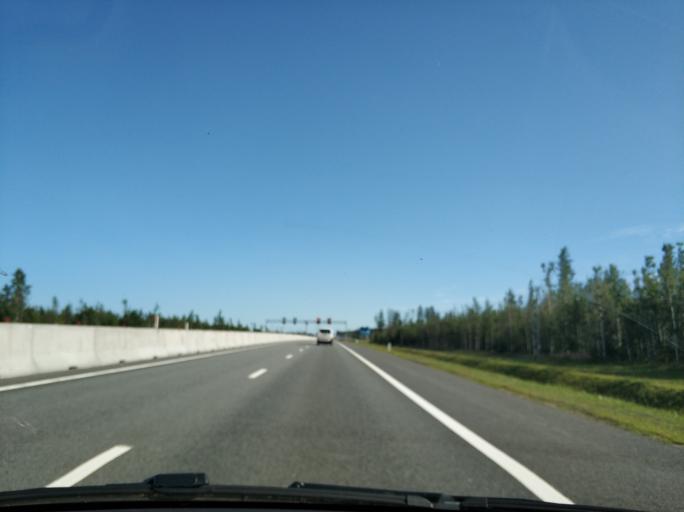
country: RU
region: Leningrad
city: Sosnovo
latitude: 60.4689
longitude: 30.1961
